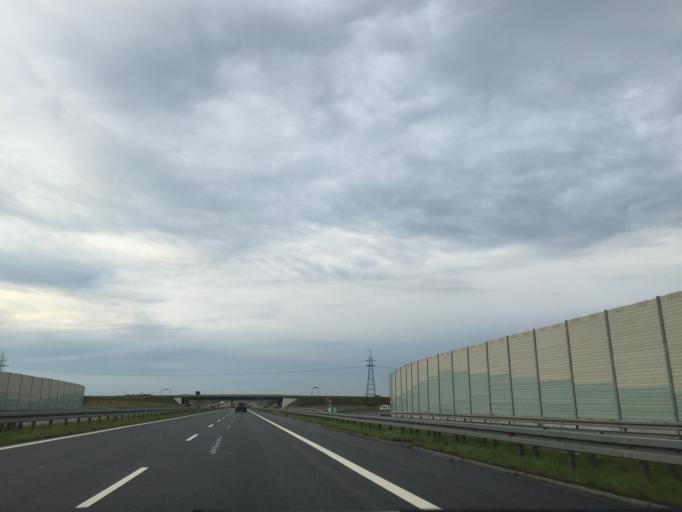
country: PL
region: Podlasie
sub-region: Powiat zambrowski
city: Zambrow
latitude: 52.9764
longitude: 22.2106
